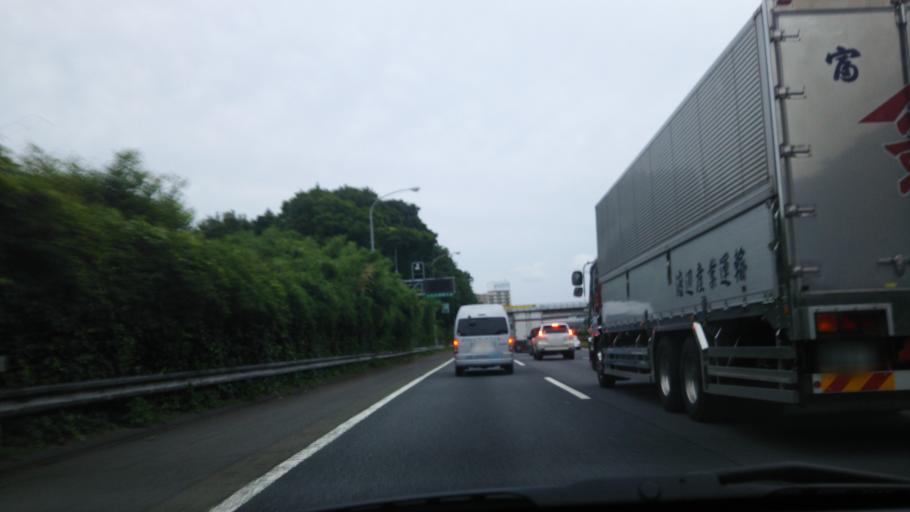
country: JP
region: Kanagawa
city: Minami-rinkan
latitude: 35.4652
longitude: 139.4358
